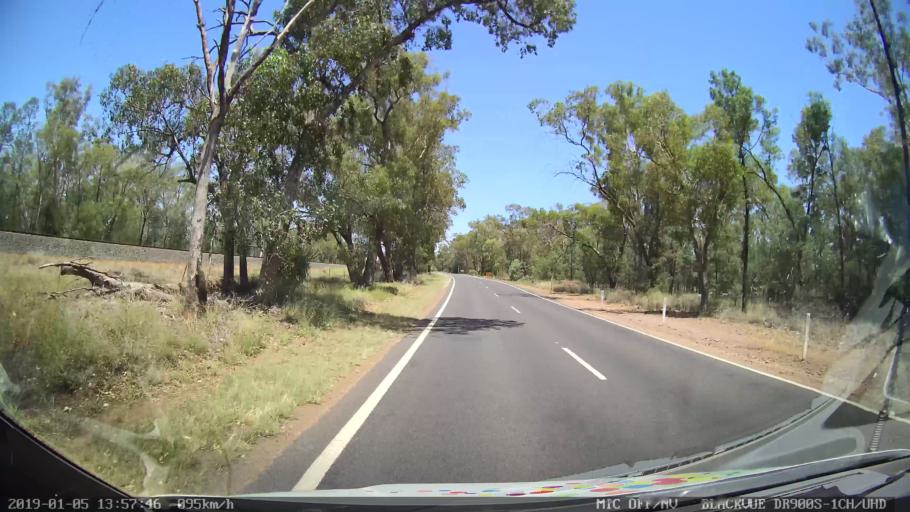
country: AU
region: New South Wales
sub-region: Gunnedah
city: Gunnedah
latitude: -31.1315
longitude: 150.2768
